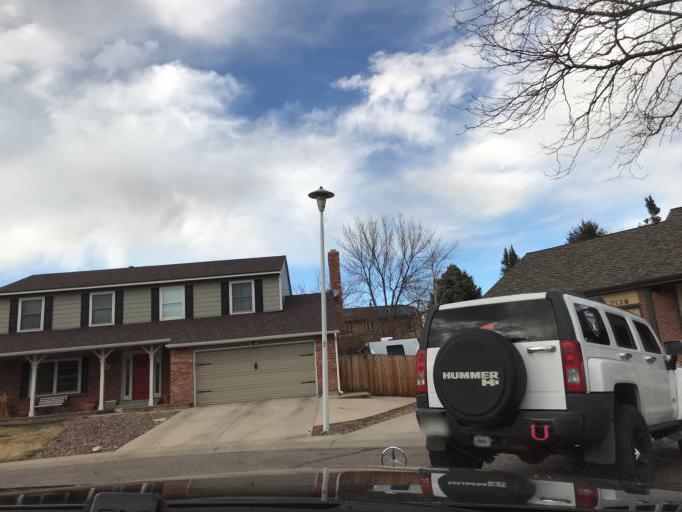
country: US
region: Colorado
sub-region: Jefferson County
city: Applewood
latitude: 39.8257
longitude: -105.1615
